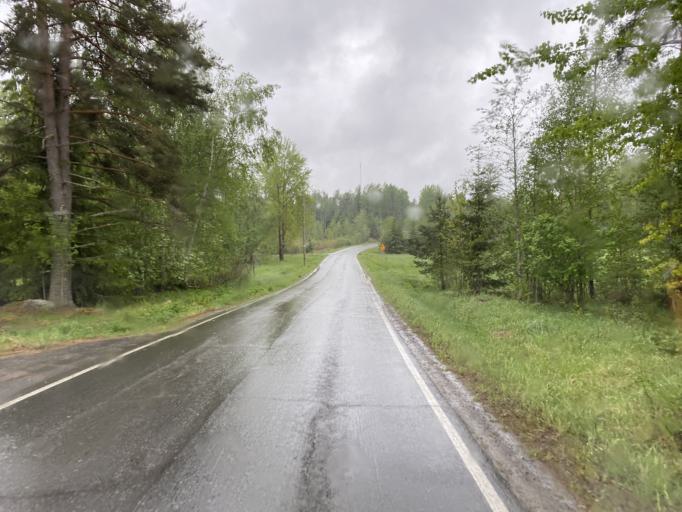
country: FI
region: Haeme
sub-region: Forssa
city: Humppila
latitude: 61.0802
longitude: 23.3116
